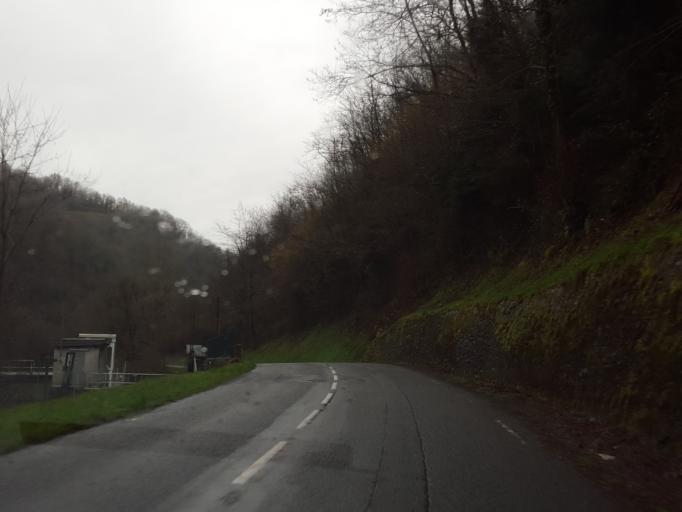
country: FR
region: Midi-Pyrenees
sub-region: Departement de l'Ariege
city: Saint-Girons
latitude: 42.9111
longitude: 1.2091
